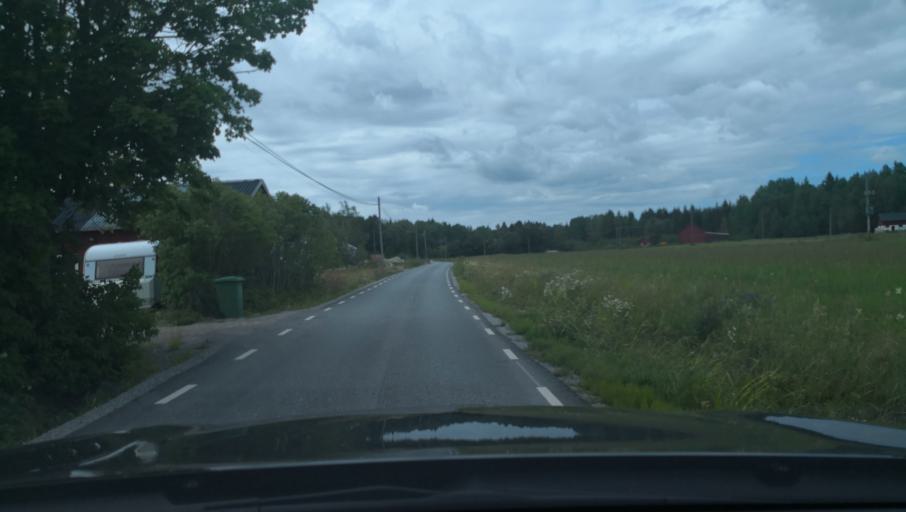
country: SE
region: Vaestmanland
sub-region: Hallstahammars Kommun
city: Hallstahammar
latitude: 59.6163
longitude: 16.1427
